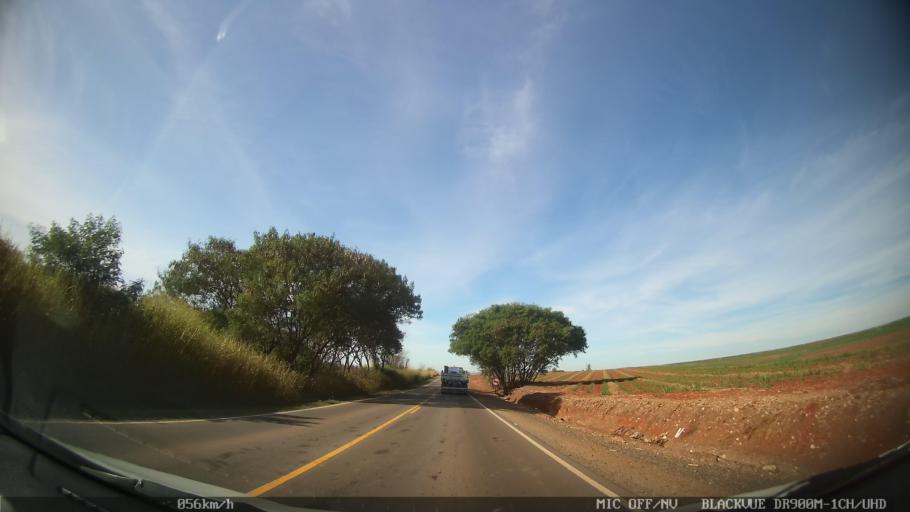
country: BR
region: Sao Paulo
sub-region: Piracicaba
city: Piracicaba
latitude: -22.7860
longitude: -47.6490
